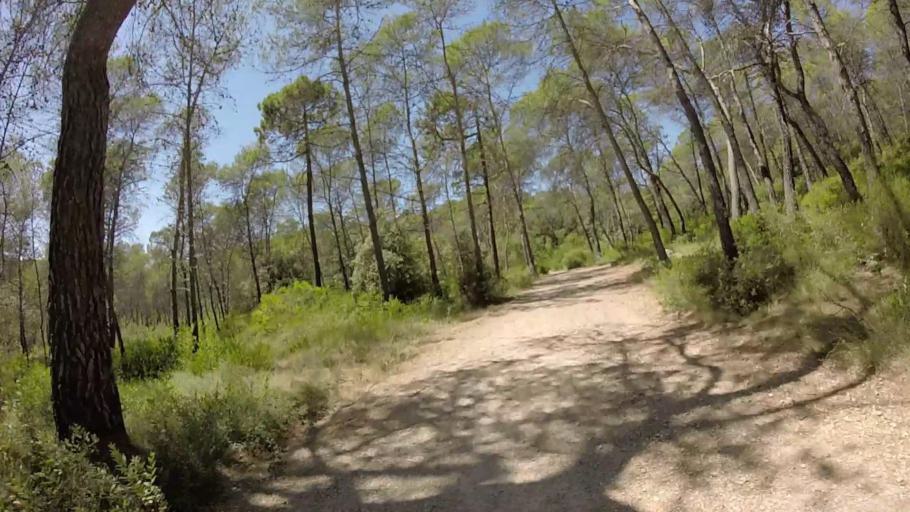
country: FR
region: Provence-Alpes-Cote d'Azur
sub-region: Departement des Alpes-Maritimes
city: Vallauris
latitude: 43.6083
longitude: 7.0462
